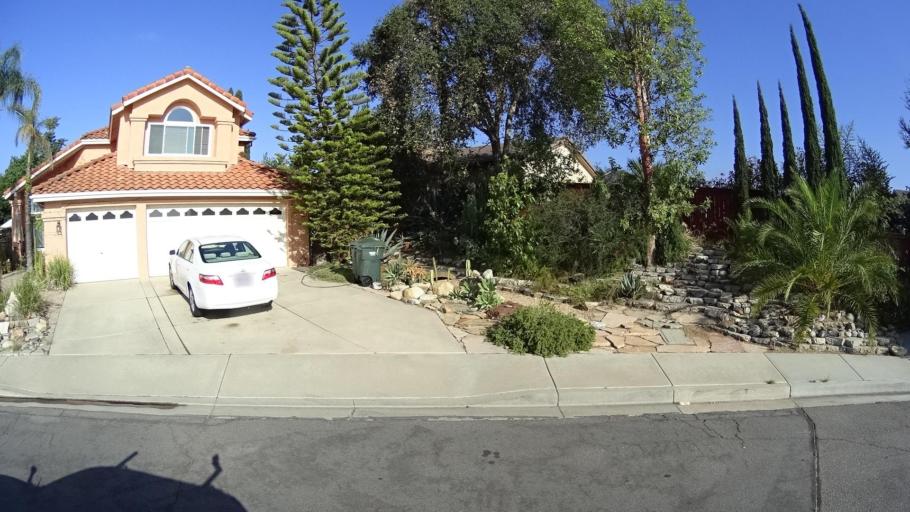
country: US
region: California
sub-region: San Diego County
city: Fallbrook
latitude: 33.3805
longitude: -117.2385
